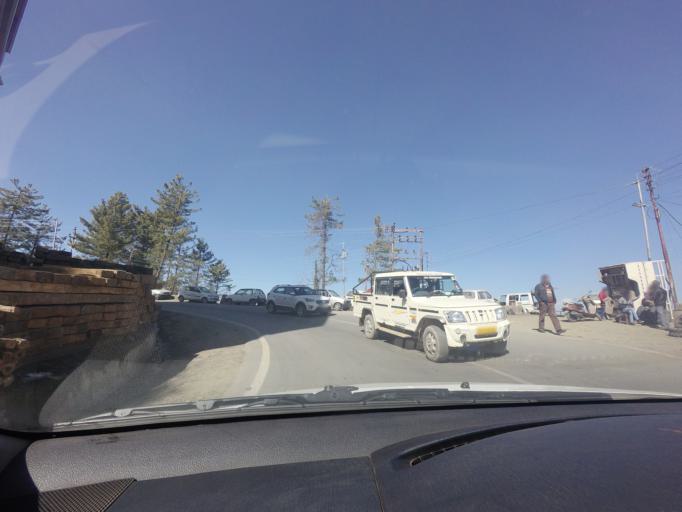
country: IN
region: Himachal Pradesh
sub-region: Shimla
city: Shimla
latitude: 31.1089
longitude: 77.2073
